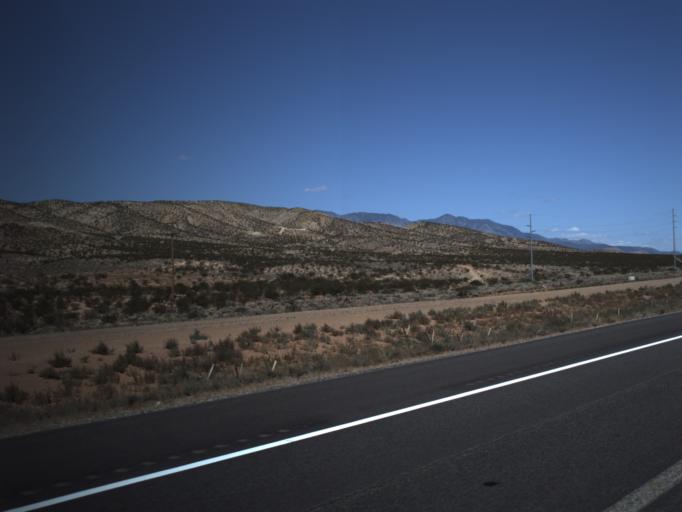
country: US
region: Utah
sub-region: Washington County
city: Washington
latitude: 37.0900
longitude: -113.4729
